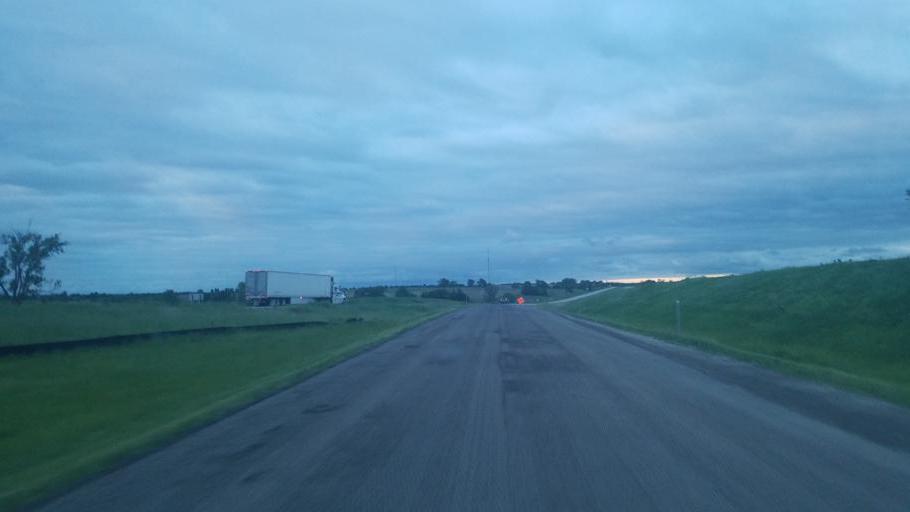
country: US
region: Iowa
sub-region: Decatur County
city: Lamoni
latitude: 40.5767
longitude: -93.9350
